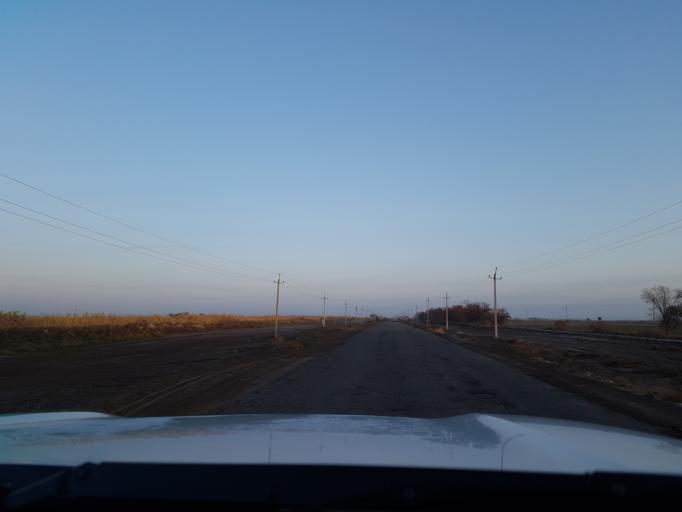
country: TM
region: Dasoguz
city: Koeneuergench
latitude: 41.8353
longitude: 58.7042
